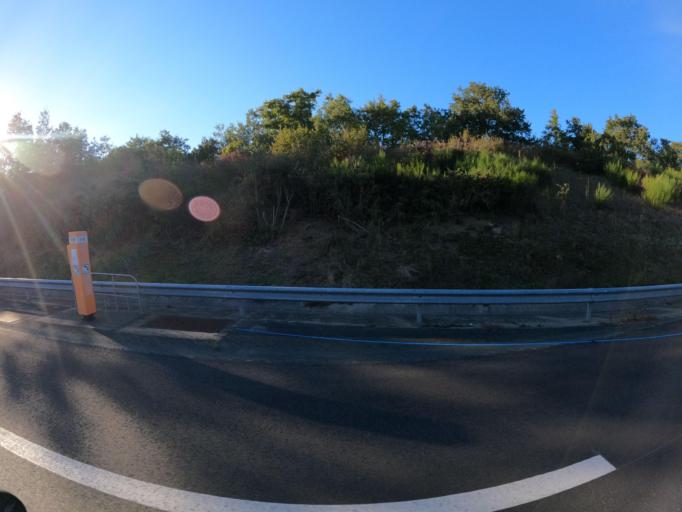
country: FR
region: Pays de la Loire
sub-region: Departement de la Vendee
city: La Gaubretiere
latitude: 46.9178
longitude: -1.0389
